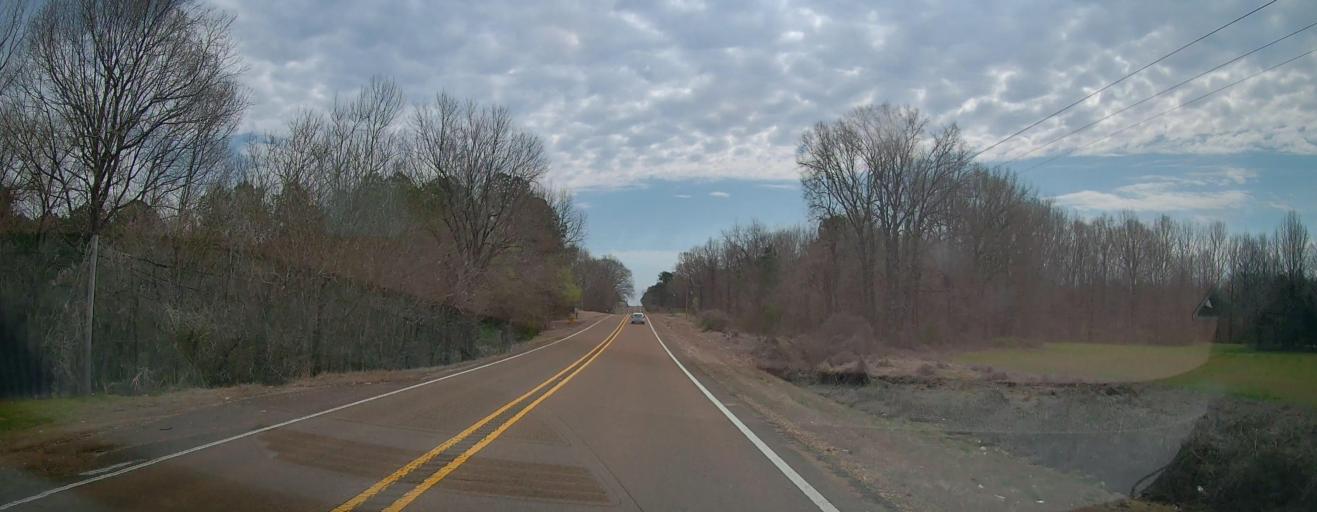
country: US
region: Mississippi
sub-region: Marshall County
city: Holly Springs
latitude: 34.8203
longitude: -89.5416
